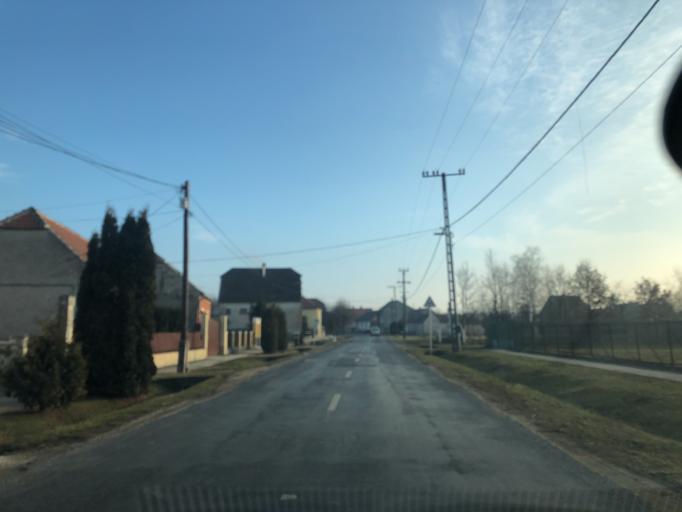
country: HU
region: Gyor-Moson-Sopron
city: Kapuvar
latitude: 47.6028
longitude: 17.0834
